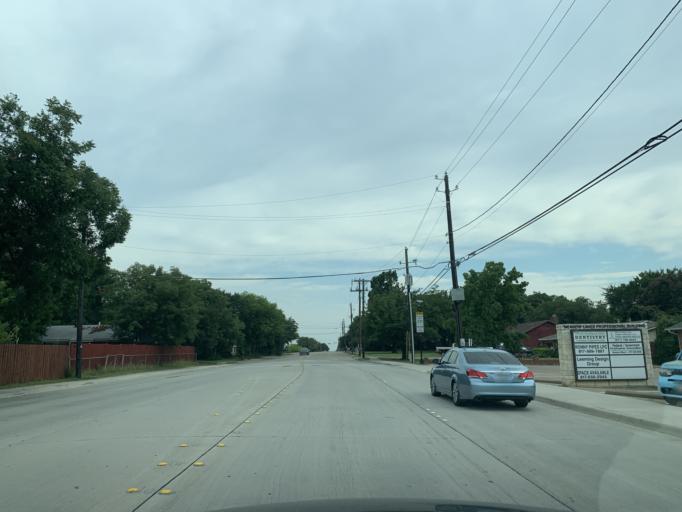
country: US
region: Texas
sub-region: Tarrant County
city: North Richland Hills
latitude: 32.8378
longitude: -97.2388
